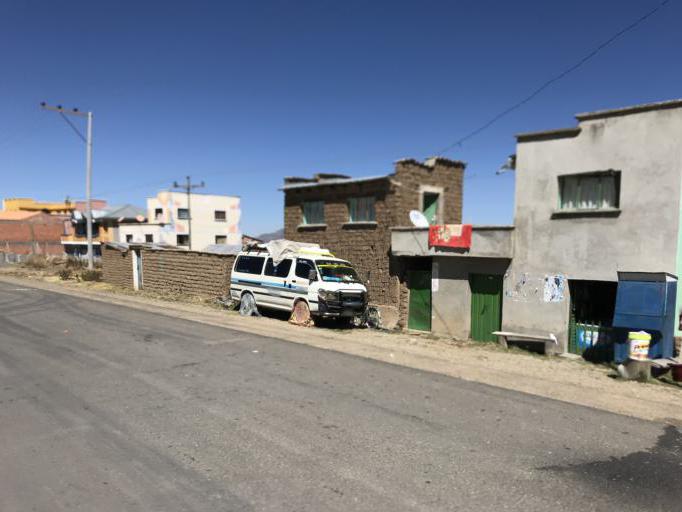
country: BO
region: La Paz
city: Huatajata
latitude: -16.2019
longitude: -68.7105
